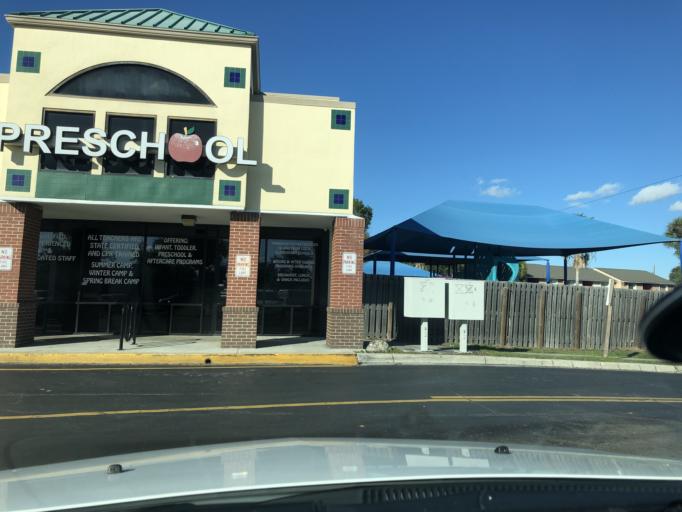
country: US
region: Florida
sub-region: Orange County
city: Oak Ridge
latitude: 28.4735
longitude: -81.4266
